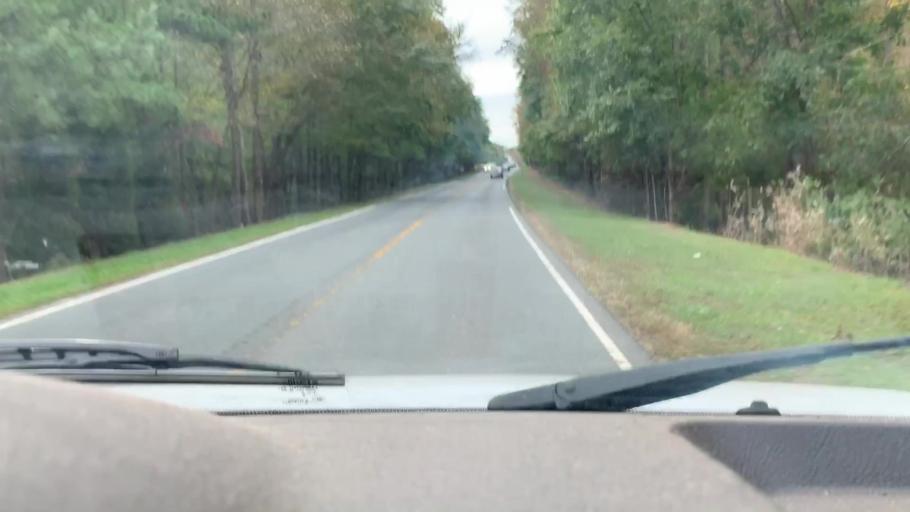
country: US
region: North Carolina
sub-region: Mecklenburg County
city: Cornelius
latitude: 35.4547
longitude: -80.8675
